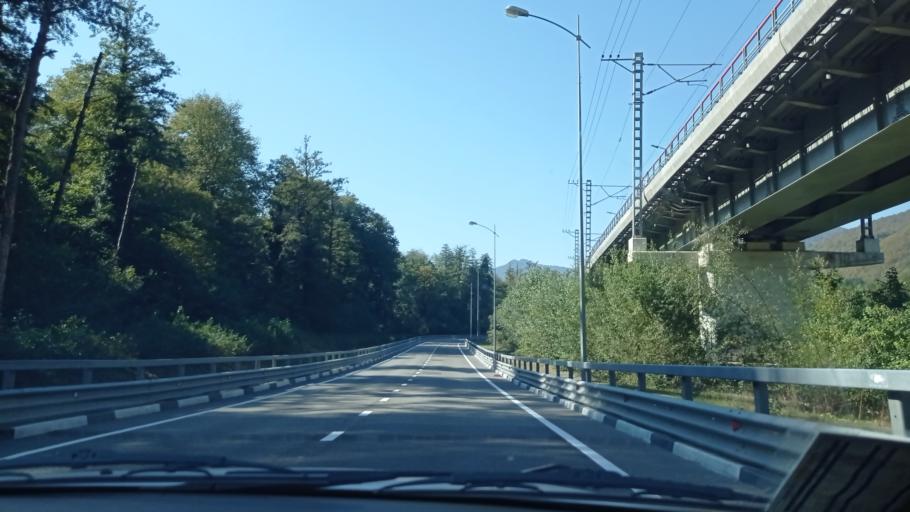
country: RU
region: Krasnodarskiy
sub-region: Sochi City
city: Krasnaya Polyana
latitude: 43.6840
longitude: 40.2429
